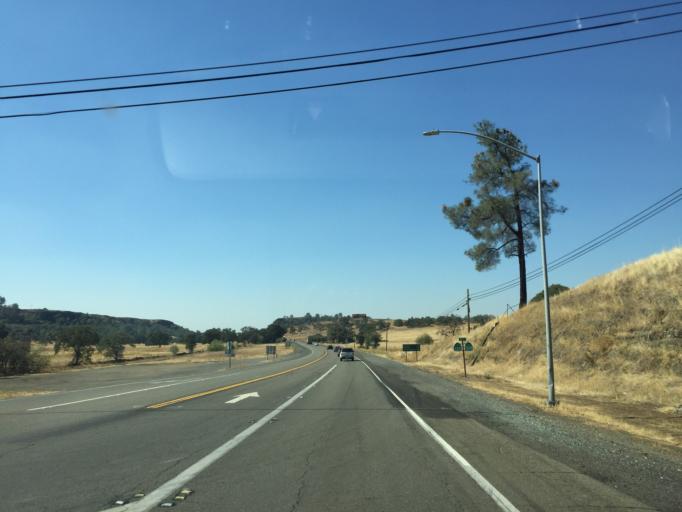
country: US
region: California
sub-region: Tuolumne County
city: Jamestown
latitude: 37.8913
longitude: -120.4881
